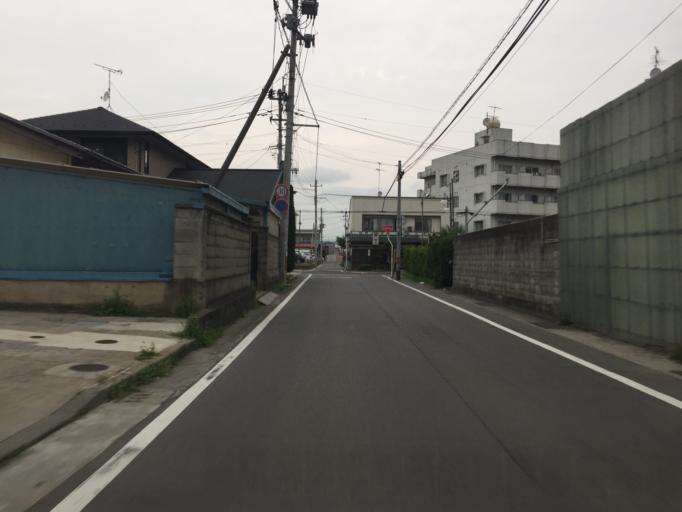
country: JP
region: Fukushima
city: Fukushima-shi
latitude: 37.7230
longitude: 140.4582
